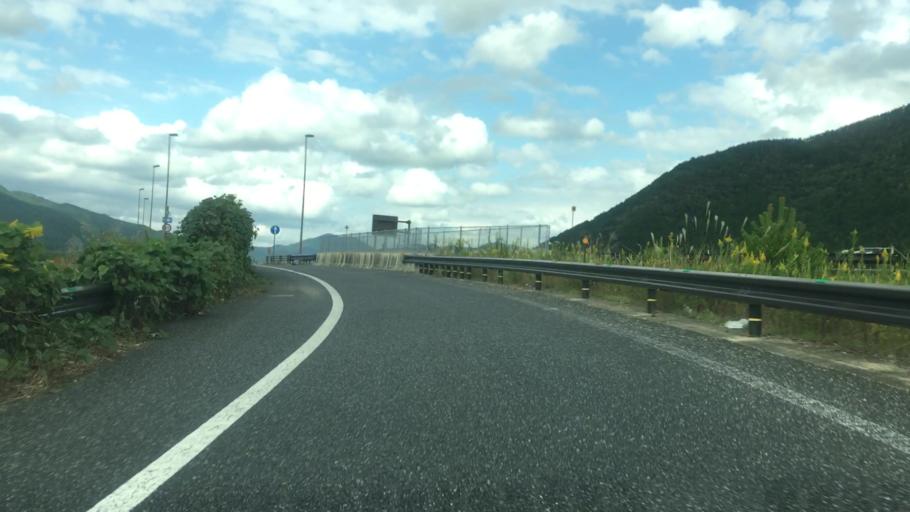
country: JP
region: Kyoto
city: Fukuchiyama
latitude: 35.1639
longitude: 135.0448
